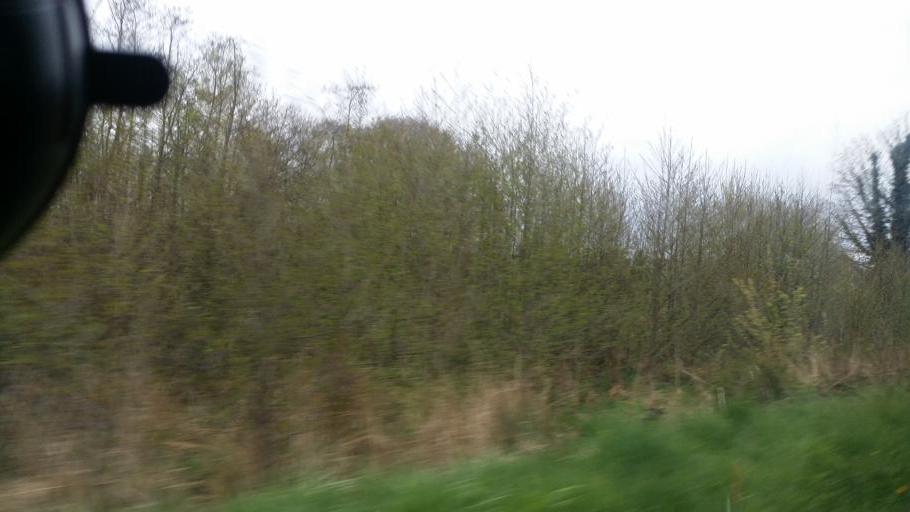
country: IE
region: Ulster
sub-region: An Cabhan
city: Belturbet
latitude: 54.0873
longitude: -7.5046
